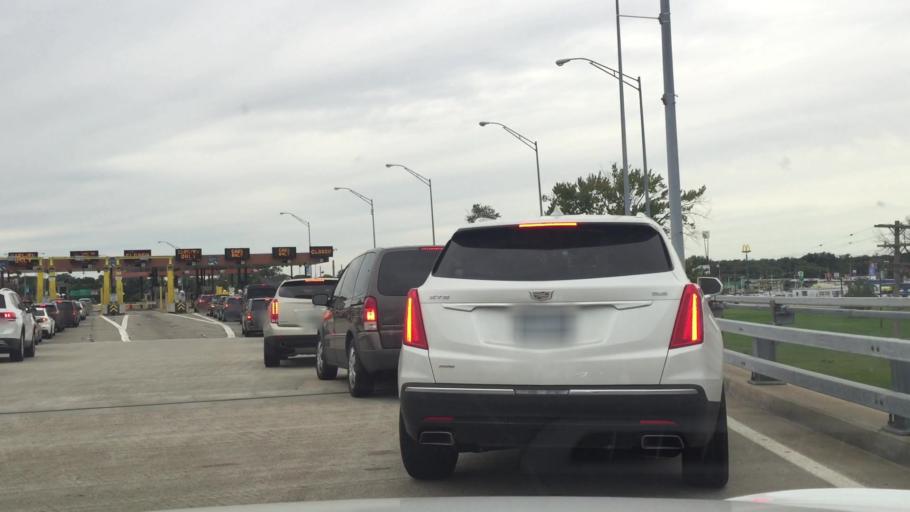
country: US
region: Michigan
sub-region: Saint Clair County
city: Port Huron
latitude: 42.9992
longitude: -82.4343
